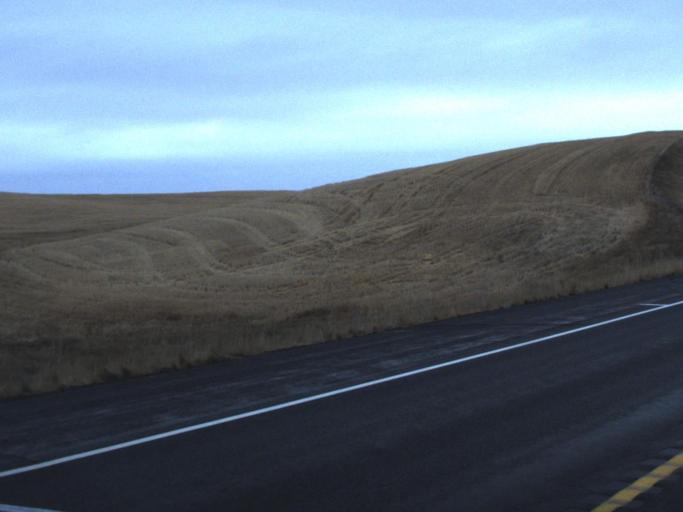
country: US
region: Washington
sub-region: Spokane County
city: Cheney
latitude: 47.3374
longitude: -117.3806
